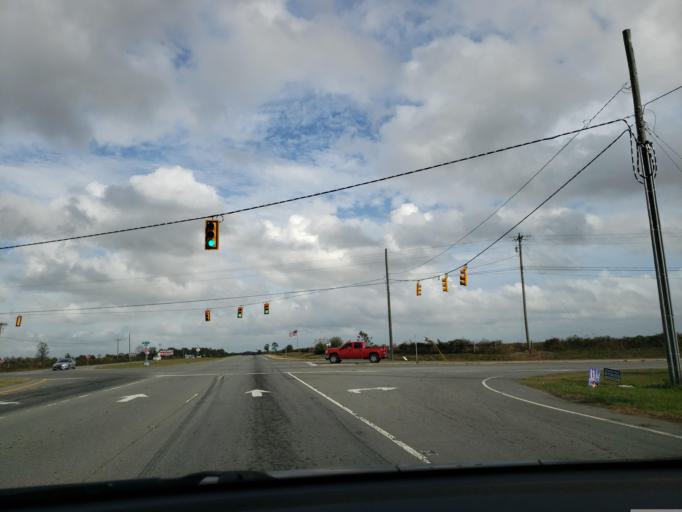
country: US
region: North Carolina
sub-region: Duplin County
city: Kenansville
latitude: 34.9348
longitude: -77.9813
